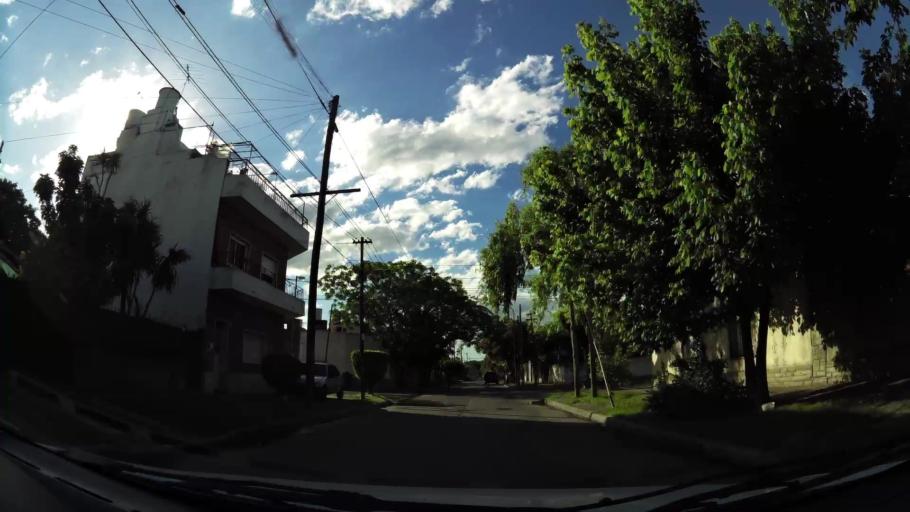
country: AR
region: Buenos Aires
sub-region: Partido de General San Martin
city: General San Martin
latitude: -34.5331
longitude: -58.5594
